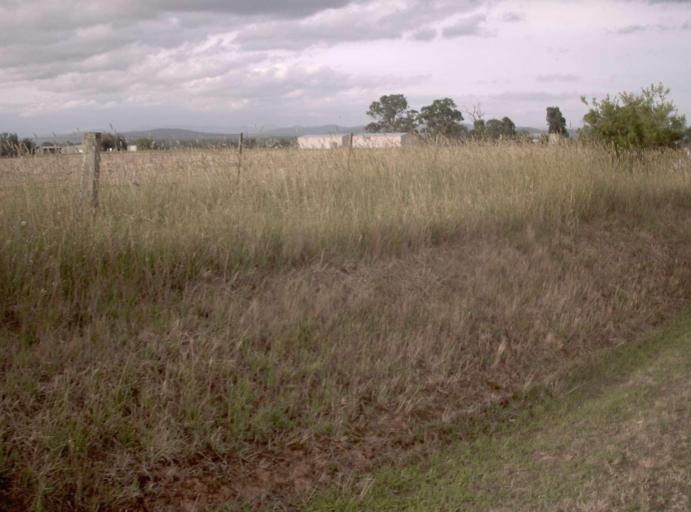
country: AU
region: Victoria
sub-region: Wellington
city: Sale
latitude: -37.8641
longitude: 147.0310
